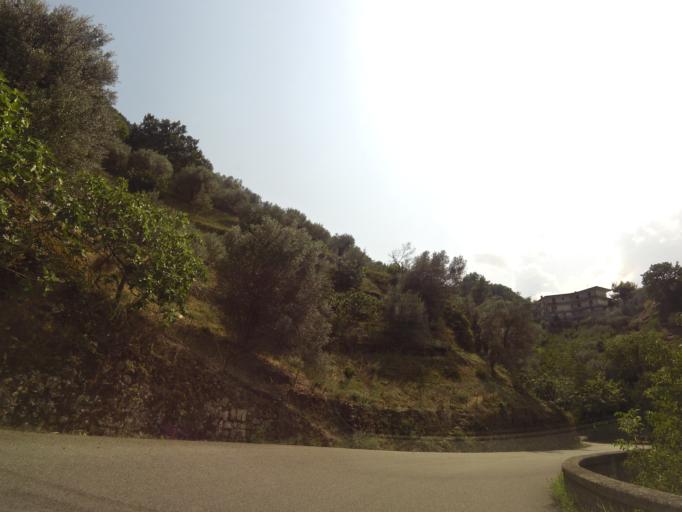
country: IT
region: Calabria
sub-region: Provincia di Reggio Calabria
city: Bivongi
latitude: 38.4807
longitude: 16.4553
